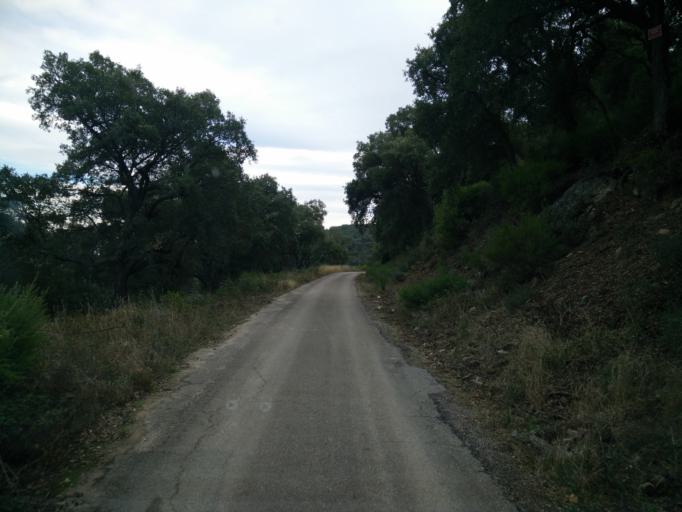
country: FR
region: Provence-Alpes-Cote d'Azur
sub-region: Departement du Var
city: Roquebrune-sur-Argens
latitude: 43.3967
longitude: 6.6088
